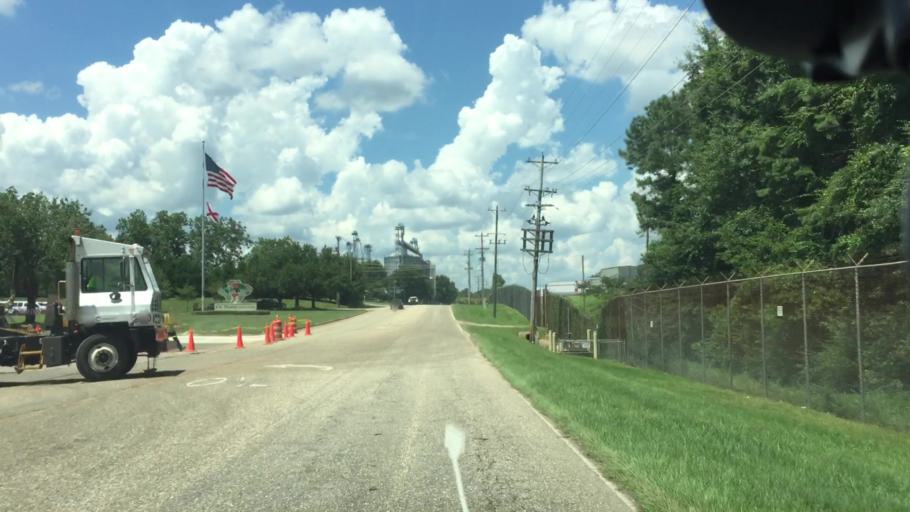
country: US
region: Alabama
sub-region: Pike County
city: Troy
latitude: 31.7802
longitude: -85.9794
